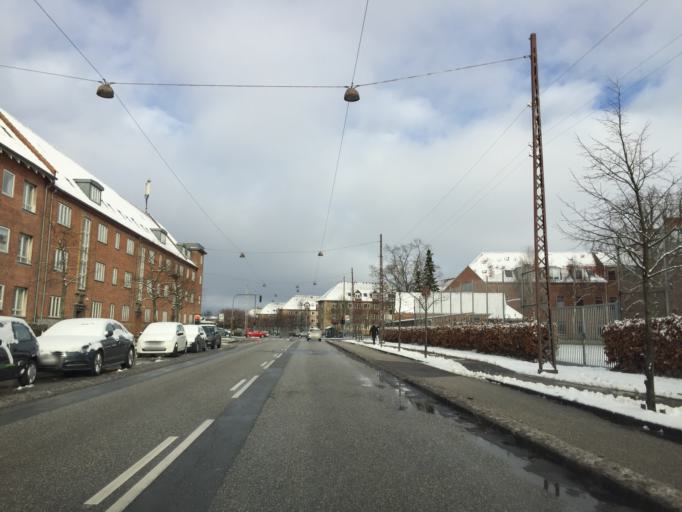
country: DK
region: Capital Region
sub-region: Tarnby Kommune
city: Tarnby
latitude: 55.6363
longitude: 12.6371
